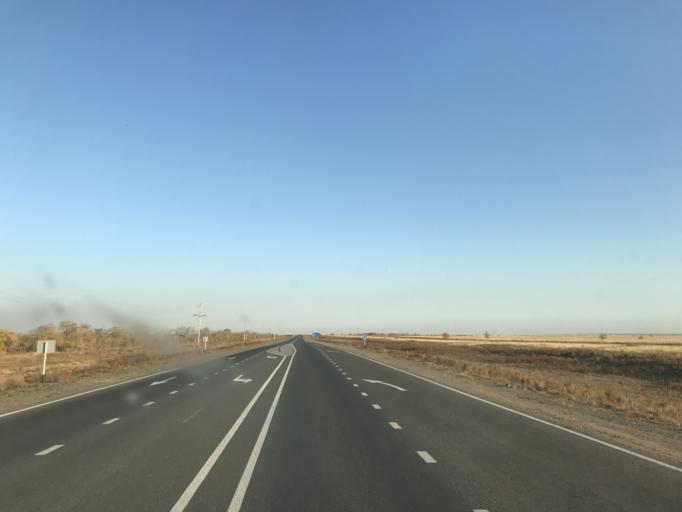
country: KZ
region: Pavlodar
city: Kurchatov
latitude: 51.0351
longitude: 79.1292
